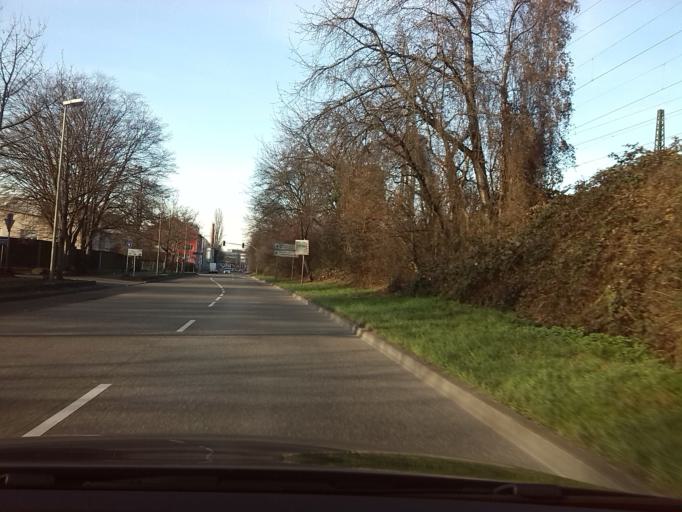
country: DE
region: Baden-Wuerttemberg
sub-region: Regierungsbezirk Stuttgart
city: Fellbach
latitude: 48.7761
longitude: 9.2555
